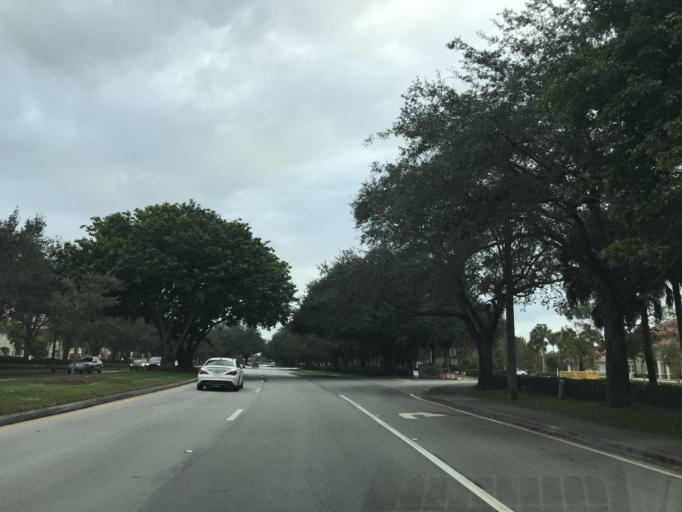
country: US
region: Florida
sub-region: Broward County
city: Parkland
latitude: 26.2990
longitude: -80.2466
